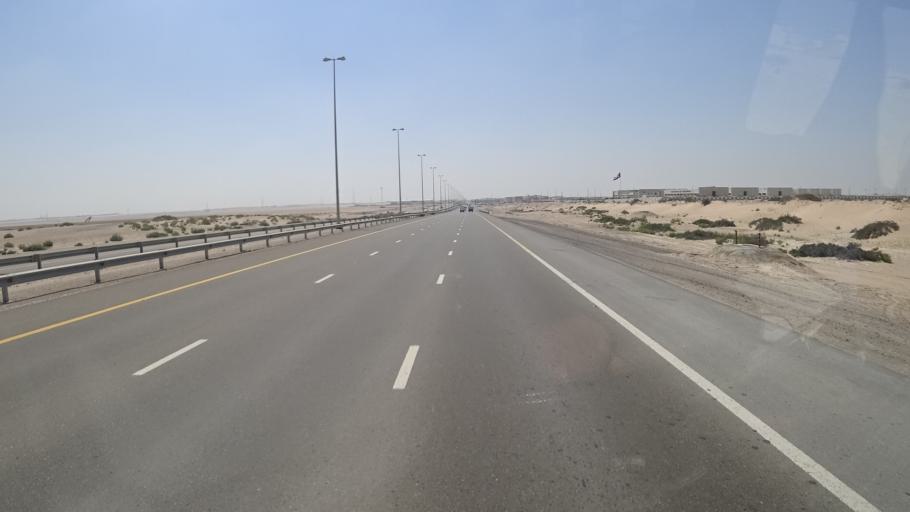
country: AE
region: Abu Dhabi
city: Abu Dhabi
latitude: 24.3250
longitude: 54.6878
